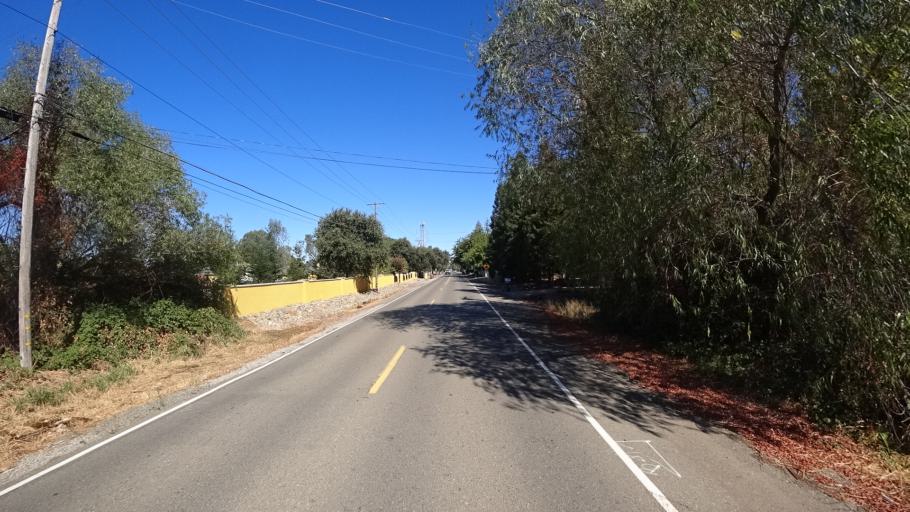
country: US
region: California
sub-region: Sacramento County
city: Vineyard
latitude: 38.4362
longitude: -121.3252
